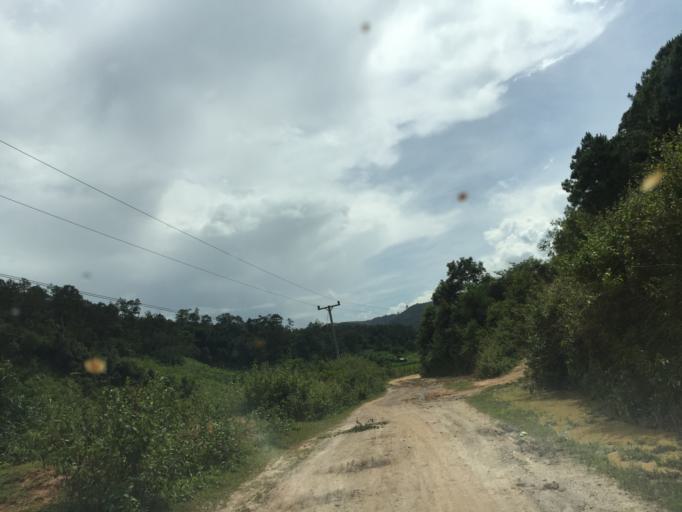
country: LA
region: Xiangkhoang
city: Muang Phonsavan
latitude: 19.3389
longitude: 103.5300
